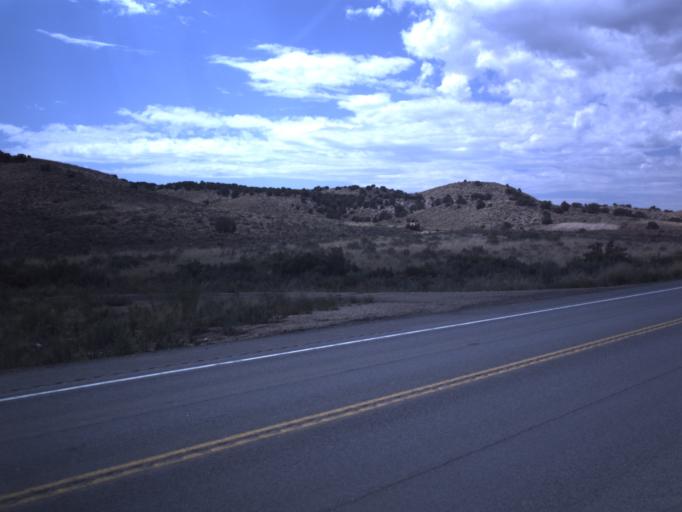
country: US
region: Utah
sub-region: Duchesne County
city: Duchesne
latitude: 40.1646
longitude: -110.4188
